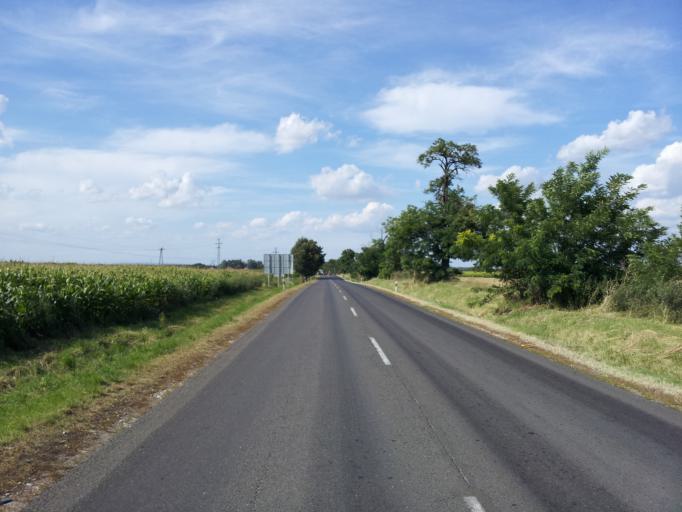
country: HU
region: Pest
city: Kiskunlachaza
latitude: 47.2219
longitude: 19.0202
